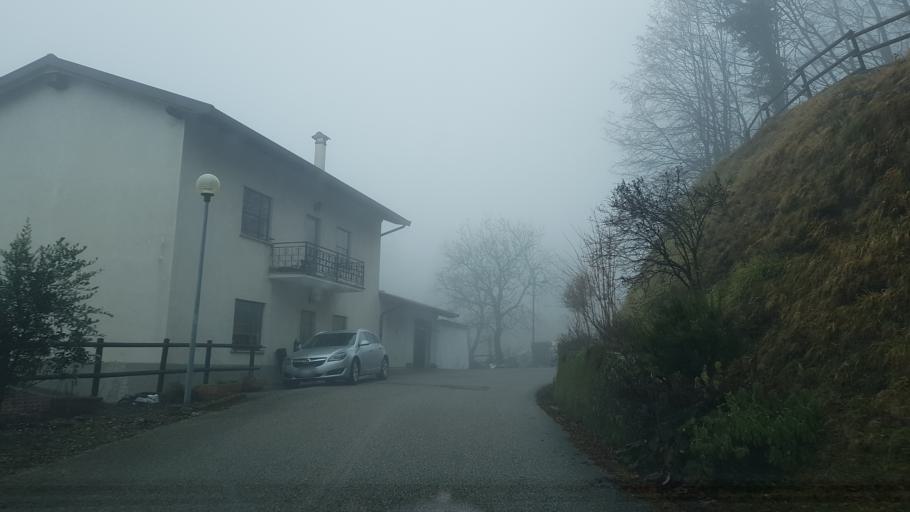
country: IT
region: Friuli Venezia Giulia
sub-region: Provincia di Udine
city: Stregna
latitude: 46.1236
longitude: 13.6028
